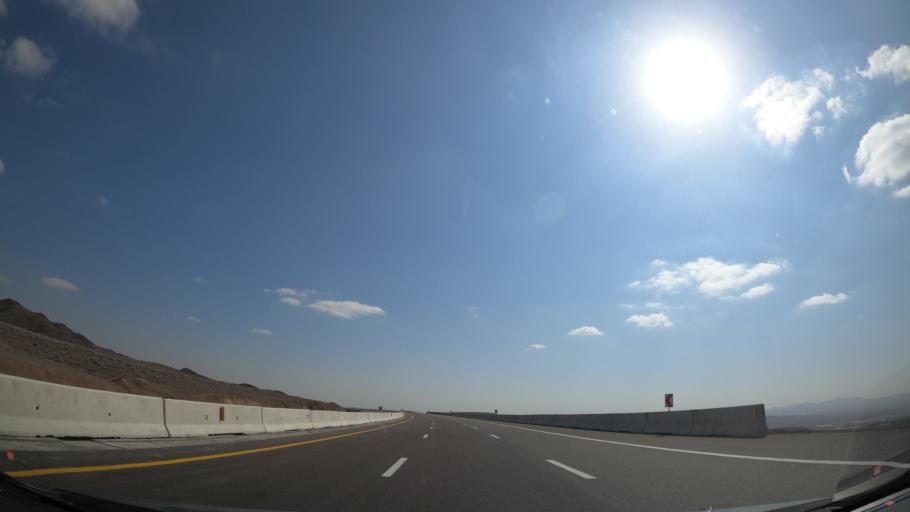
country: IR
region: Alborz
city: Eshtehard
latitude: 35.6681
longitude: 50.6465
